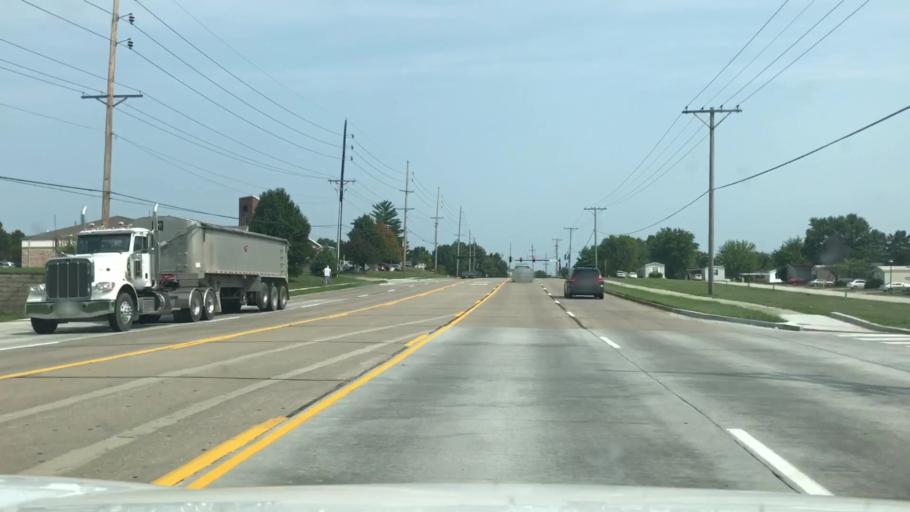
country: US
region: Missouri
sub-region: Saint Charles County
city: Dardenne Prairie
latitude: 38.7903
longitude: -90.7367
